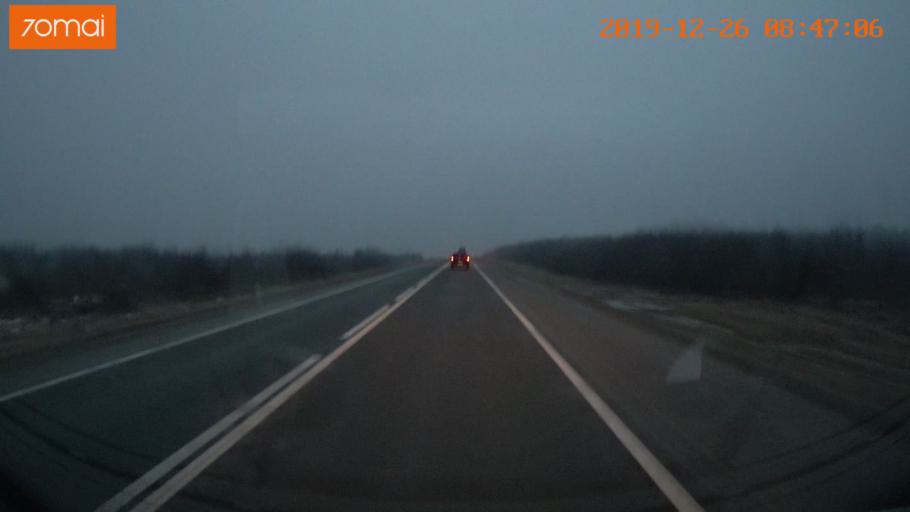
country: RU
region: Jaroslavl
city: Prechistoye
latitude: 58.6192
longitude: 40.3332
